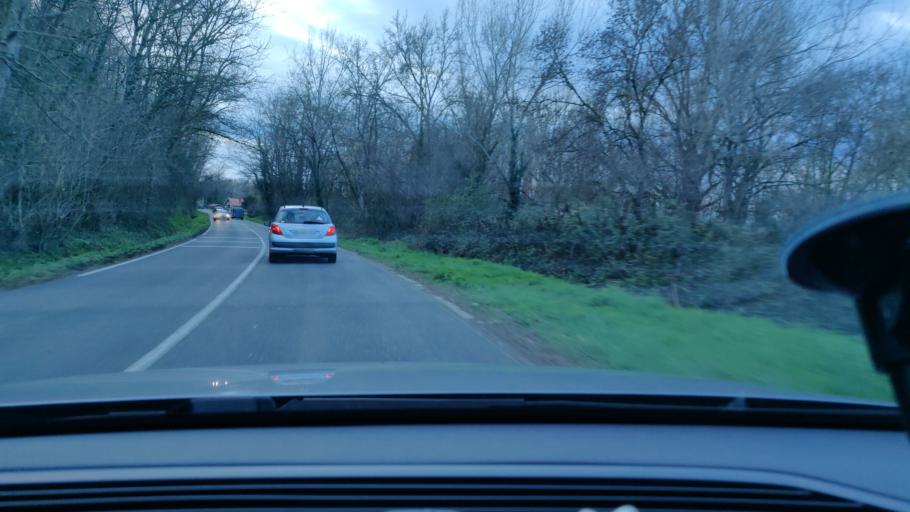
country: FR
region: Midi-Pyrenees
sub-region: Departement de la Haute-Garonne
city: Vieille-Toulouse
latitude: 43.5428
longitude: 1.4368
